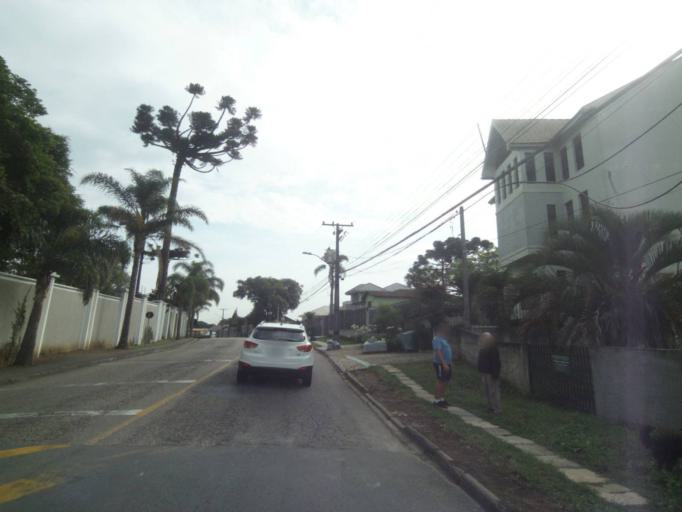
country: BR
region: Parana
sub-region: Curitiba
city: Curitiba
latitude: -25.4035
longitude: -49.3133
